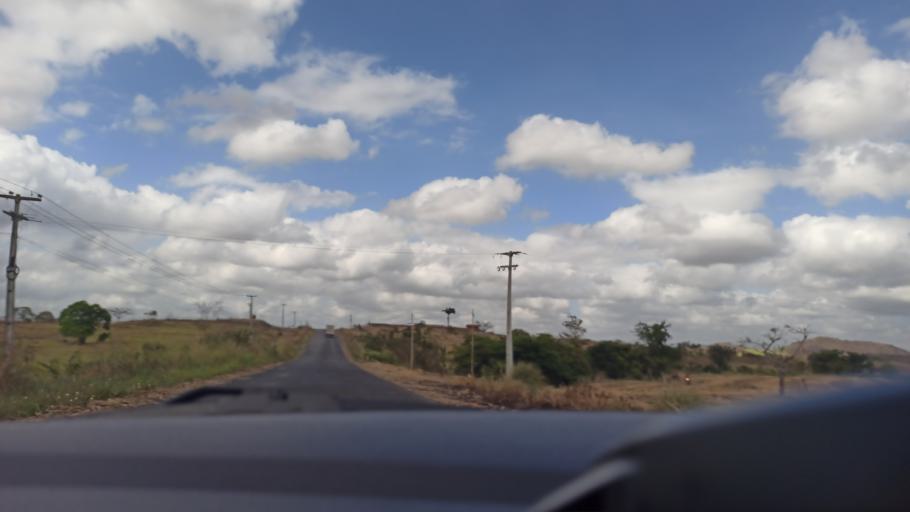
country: BR
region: Pernambuco
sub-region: Timbauba
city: Timbauba
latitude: -7.4768
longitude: -35.2817
